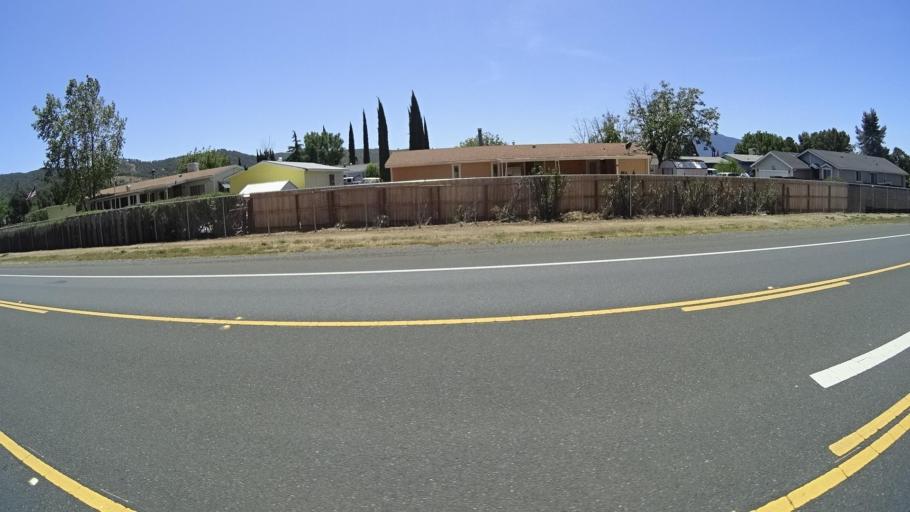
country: US
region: California
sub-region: Lake County
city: Clearlake Oaks
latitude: 39.0210
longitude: -122.6501
